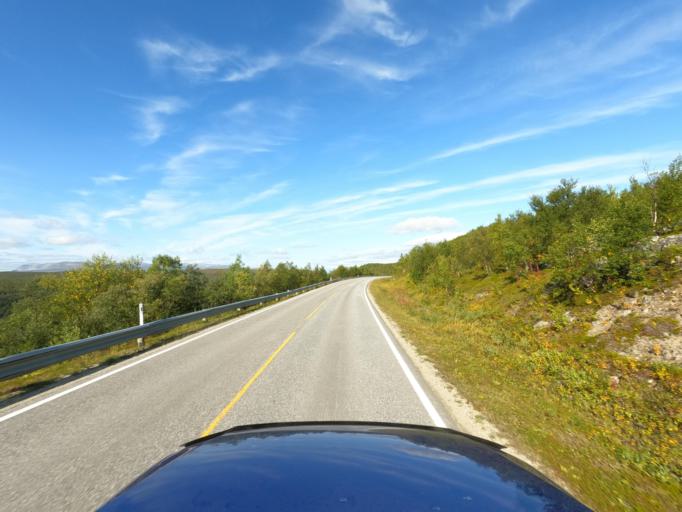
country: NO
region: Finnmark Fylke
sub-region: Porsanger
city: Lakselv
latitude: 69.7694
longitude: 25.1679
